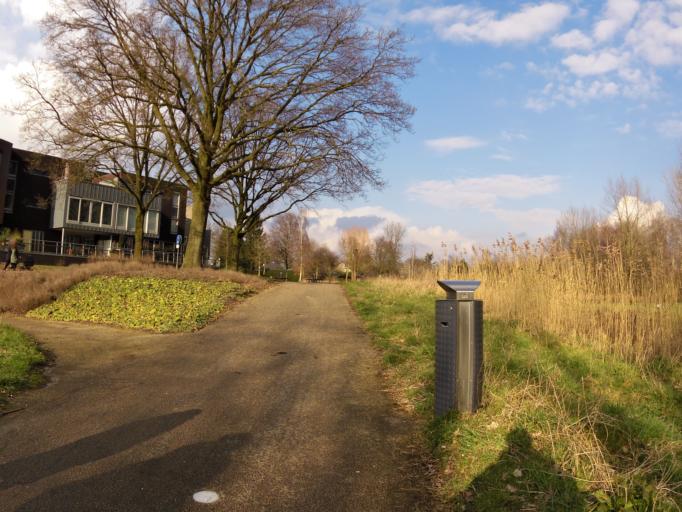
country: NL
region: North Brabant
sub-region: Gemeente Boxtel
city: Boxtel
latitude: 51.5971
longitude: 5.3191
